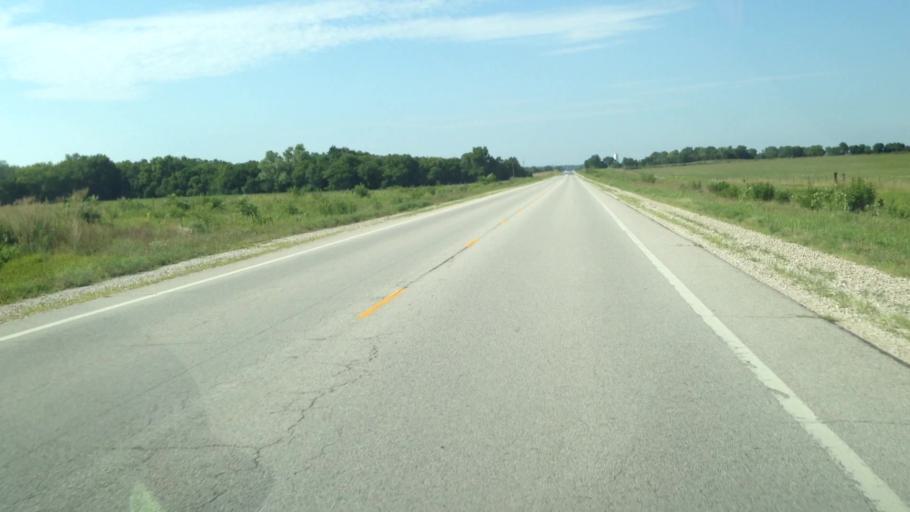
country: US
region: Kansas
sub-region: Neosho County
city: Erie
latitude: 37.4886
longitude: -95.2692
